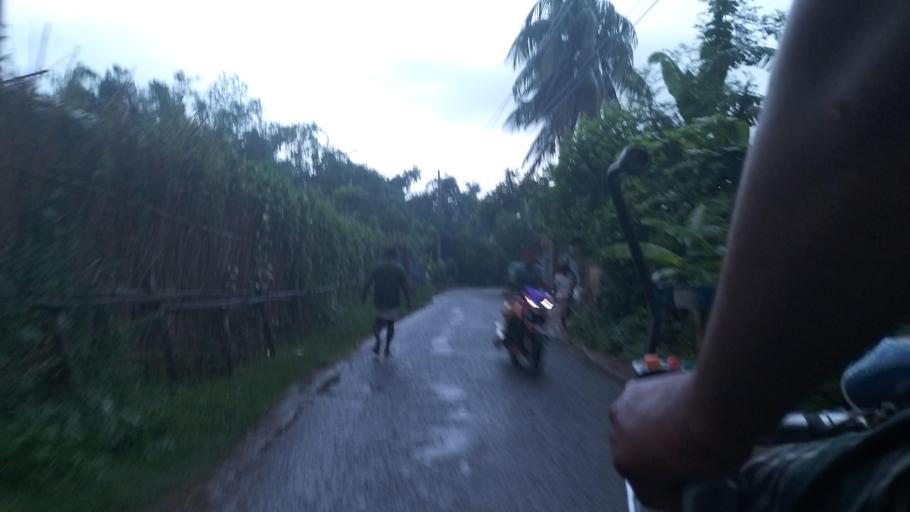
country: BD
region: Rajshahi
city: Rajshahi
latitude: 24.5448
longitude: 88.6310
